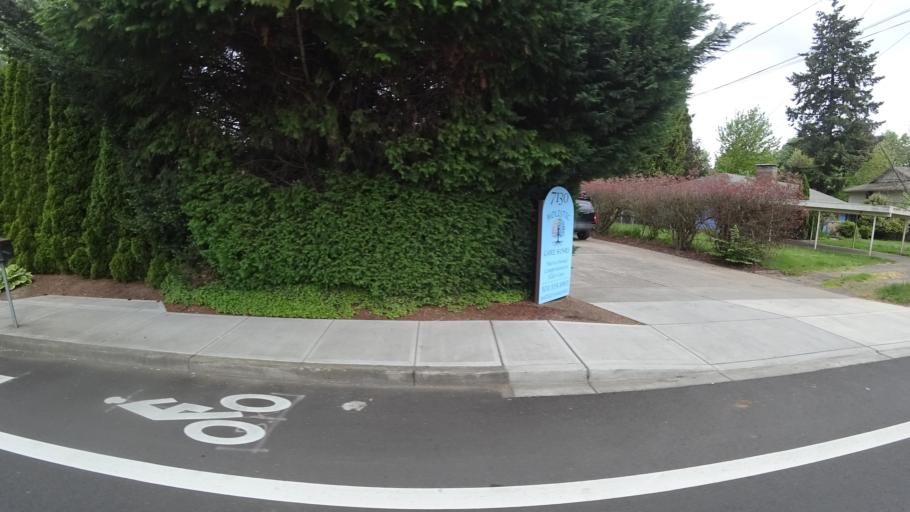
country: US
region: Oregon
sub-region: Washington County
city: Garden Home-Whitford
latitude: 45.4684
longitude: -122.7763
